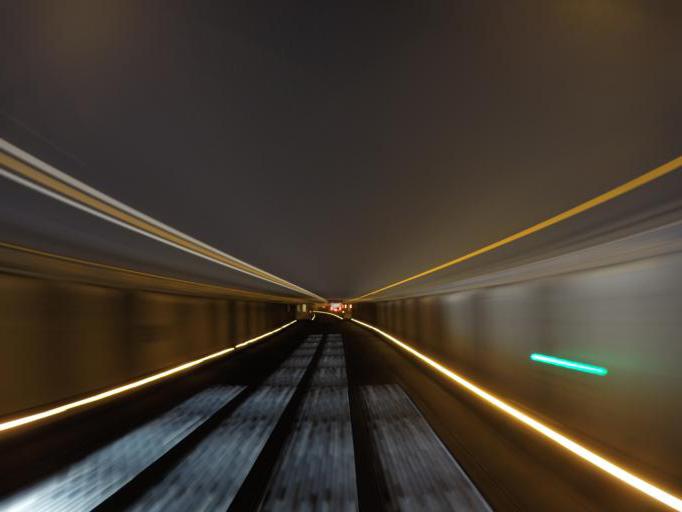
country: ZA
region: Western Cape
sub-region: Cape Winelands District Municipality
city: Paarl
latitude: -33.7347
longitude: 19.0714
